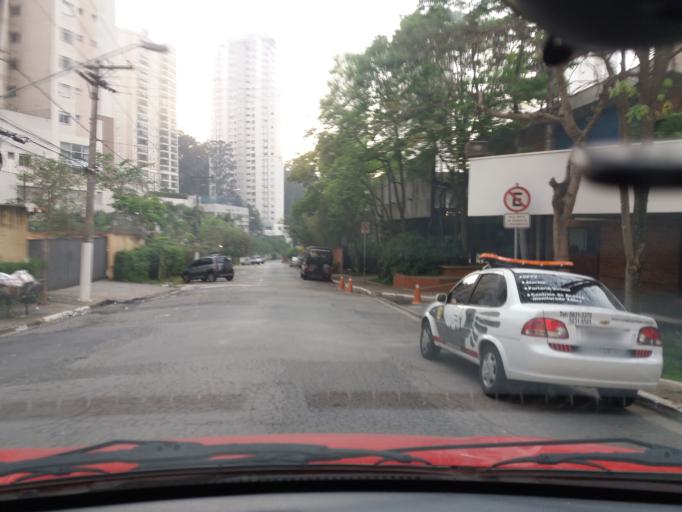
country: BR
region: Sao Paulo
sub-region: Taboao Da Serra
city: Taboao da Serra
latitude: -23.6289
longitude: -46.7417
